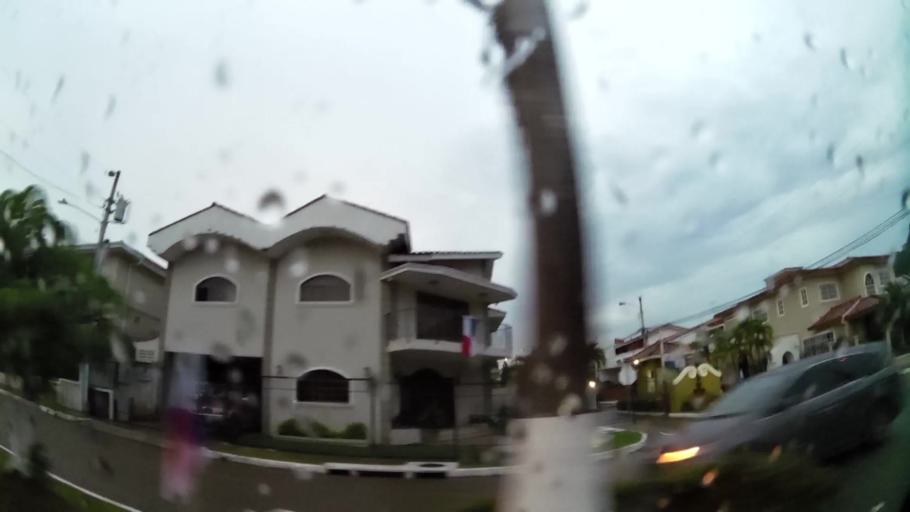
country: PA
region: Panama
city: Las Cumbres
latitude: 9.0431
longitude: -79.5239
